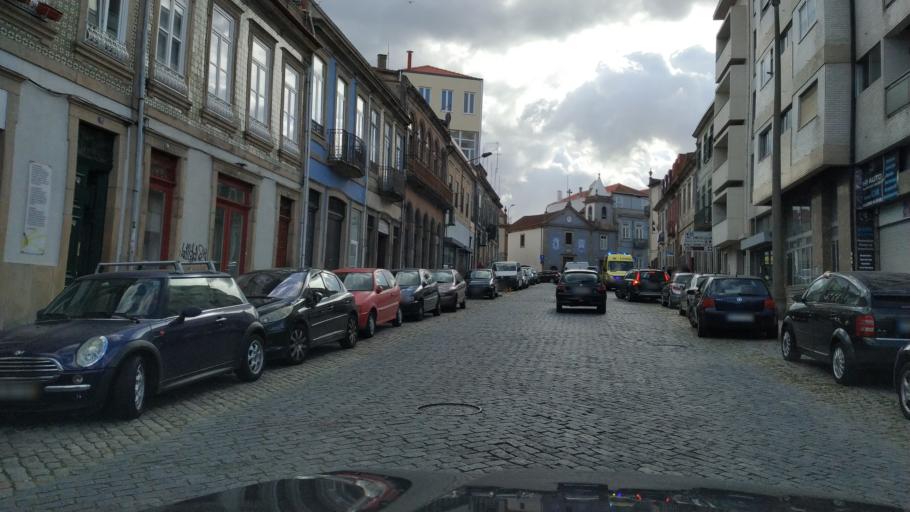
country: PT
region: Porto
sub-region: Porto
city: Porto
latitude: 41.1479
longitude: -8.5887
